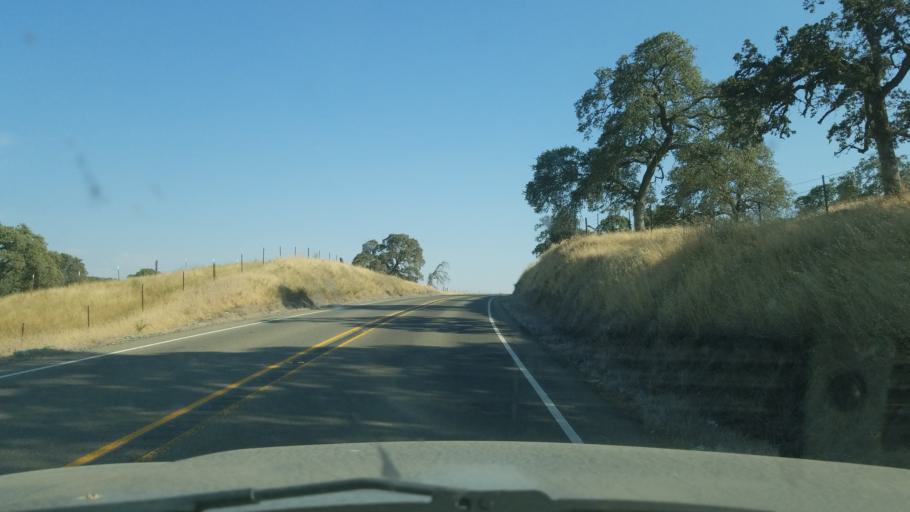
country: US
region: California
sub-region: Tuolumne County
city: Jamestown
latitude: 37.8182
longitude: -120.4728
